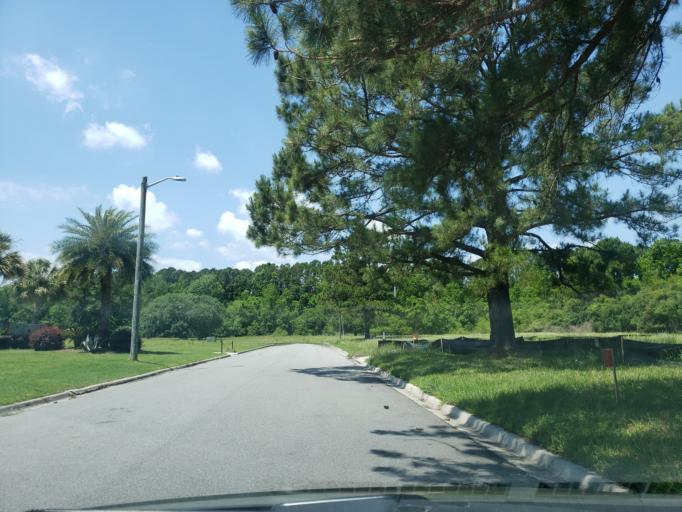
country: US
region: Georgia
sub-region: Chatham County
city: Isle of Hope
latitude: 31.9790
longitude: -81.0821
